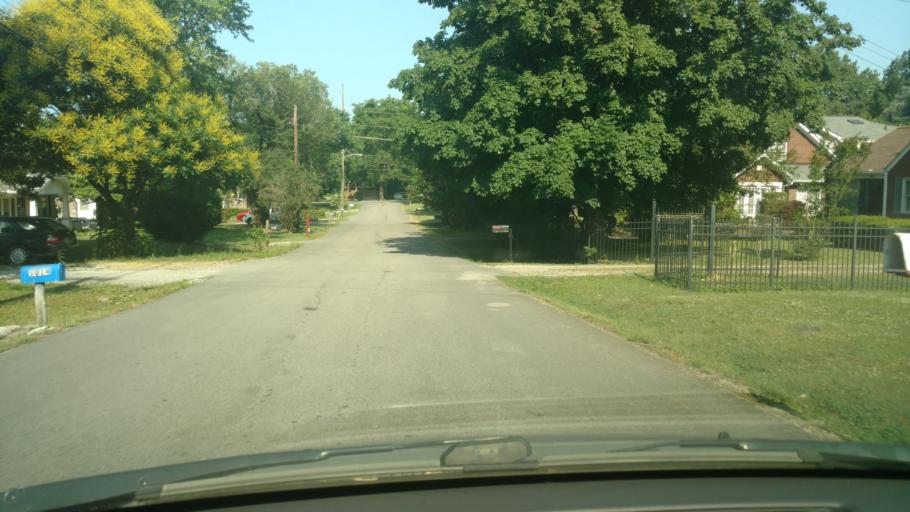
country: US
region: Tennessee
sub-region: Davidson County
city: Nashville
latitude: 36.2239
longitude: -86.7283
